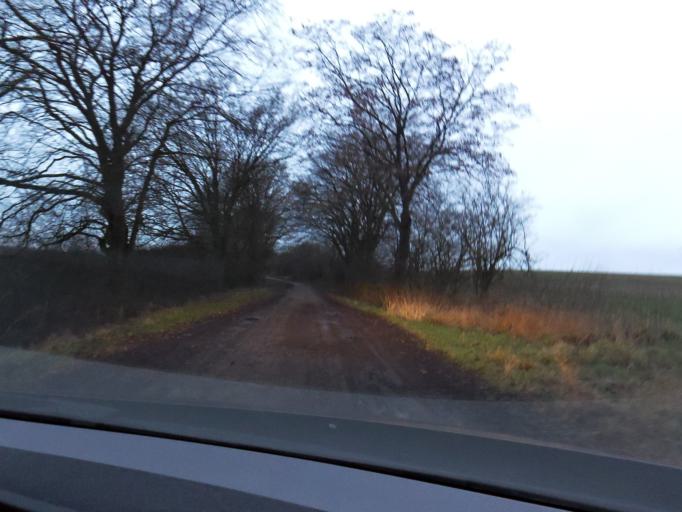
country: DE
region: Mecklenburg-Vorpommern
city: Roggendorf
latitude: 53.6822
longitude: 10.9707
